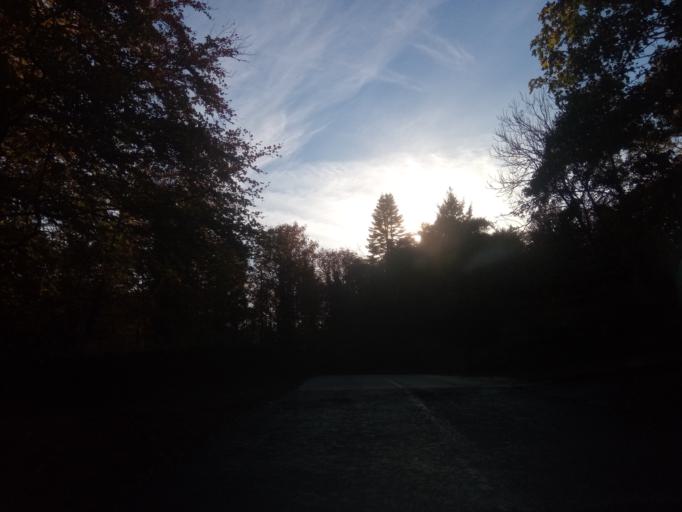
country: GB
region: Scotland
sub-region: The Scottish Borders
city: Eyemouth
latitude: 55.8516
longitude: -2.1073
